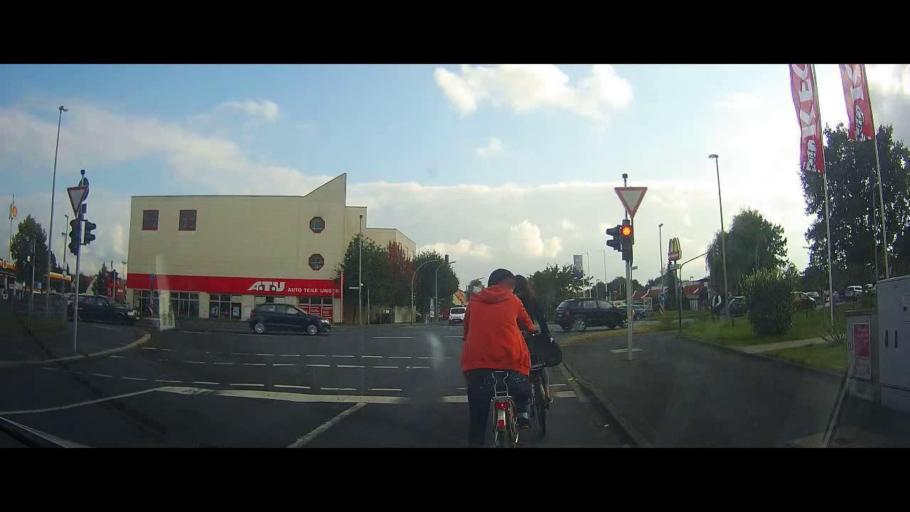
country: DE
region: Lower Saxony
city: Rosdorf
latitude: 51.5353
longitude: 9.8852
